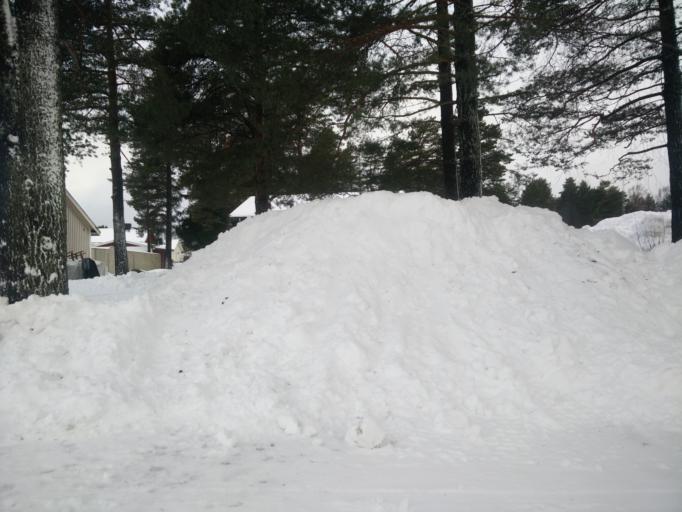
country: SE
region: Vaesternorrland
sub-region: Sundsvalls Kommun
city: Nolby
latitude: 62.2905
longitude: 17.3644
